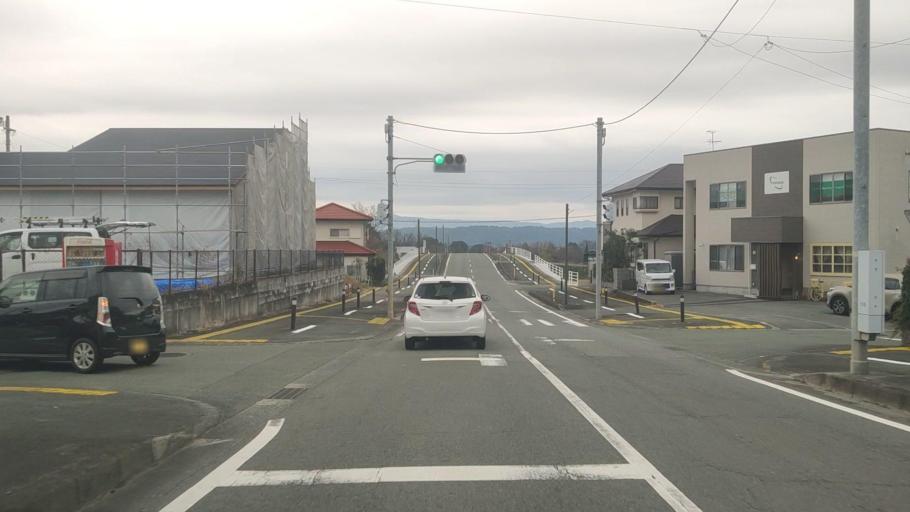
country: JP
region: Kumamoto
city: Ozu
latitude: 32.8773
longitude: 130.8939
